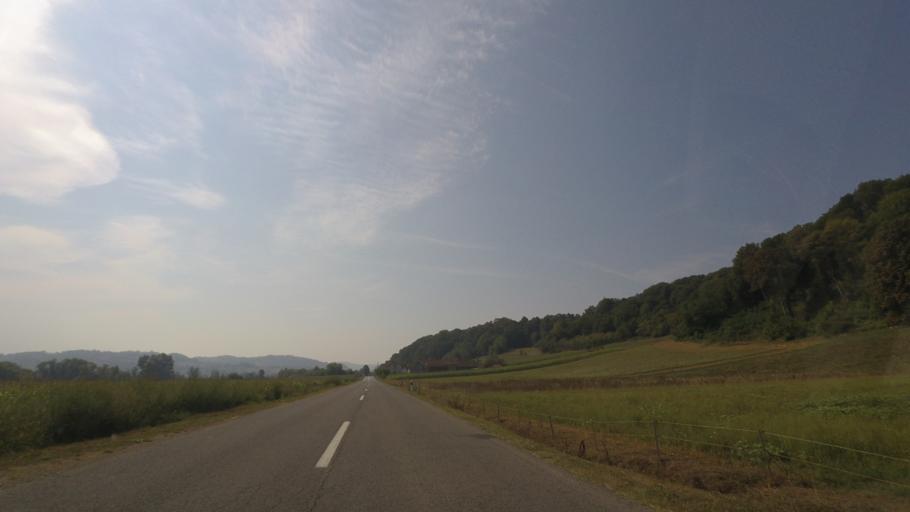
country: HR
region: Sisacko-Moslavacka
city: Dvor
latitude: 45.0802
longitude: 16.3830
